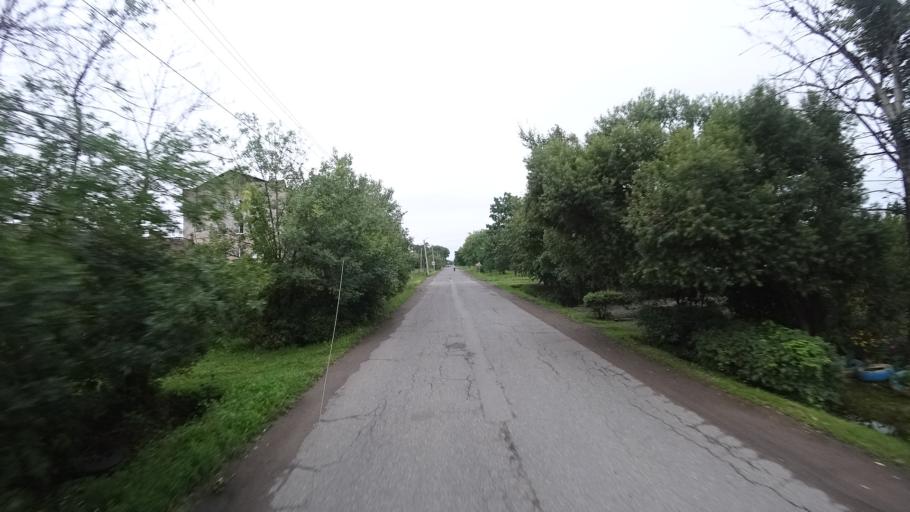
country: RU
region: Primorskiy
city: Chernigovka
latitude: 44.3398
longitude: 132.5768
